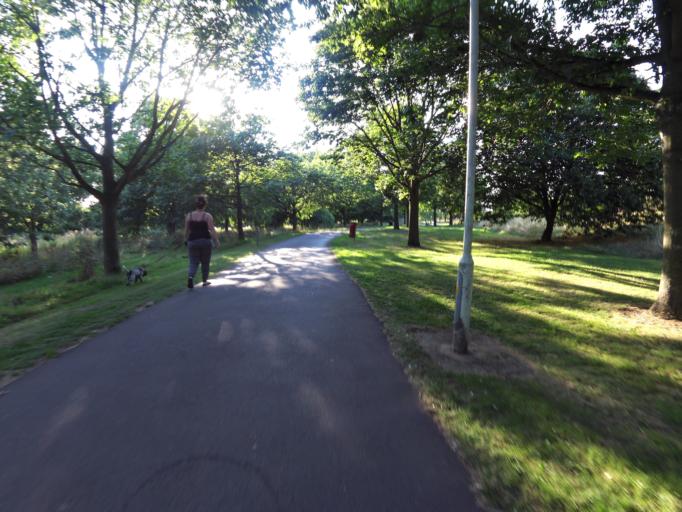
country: GB
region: England
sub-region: Essex
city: Chelmsford
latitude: 51.7331
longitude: 0.4608
